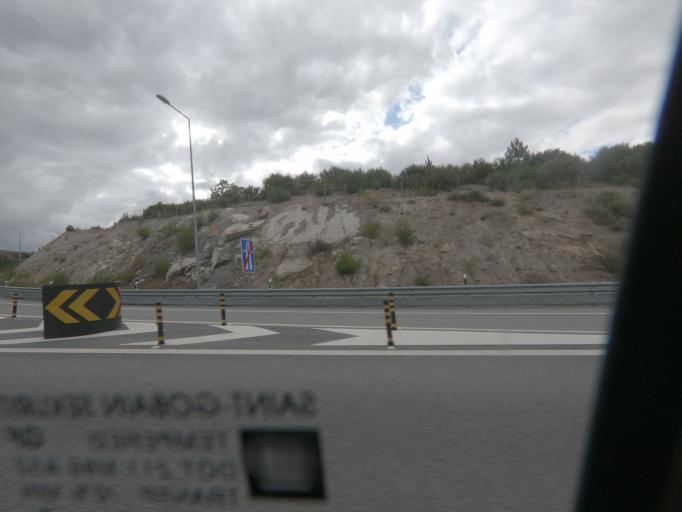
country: PT
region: Vila Real
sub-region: Vila Real
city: Vila Real
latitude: 41.2769
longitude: -7.7671
